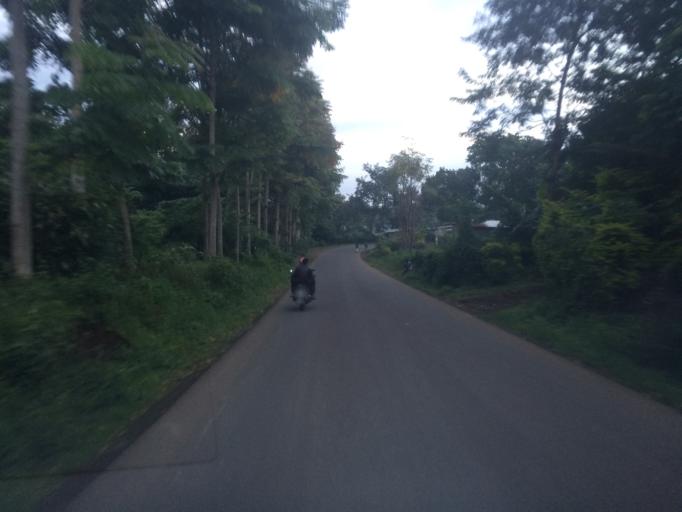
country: TZ
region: Arusha
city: Nkoaranga
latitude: -3.3617
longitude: 36.8156
